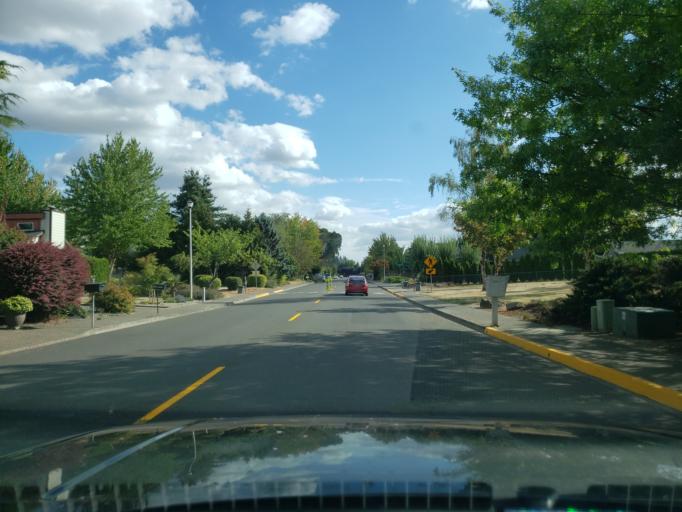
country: US
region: Oregon
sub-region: Yamhill County
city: McMinnville
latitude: 45.2051
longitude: -123.2196
